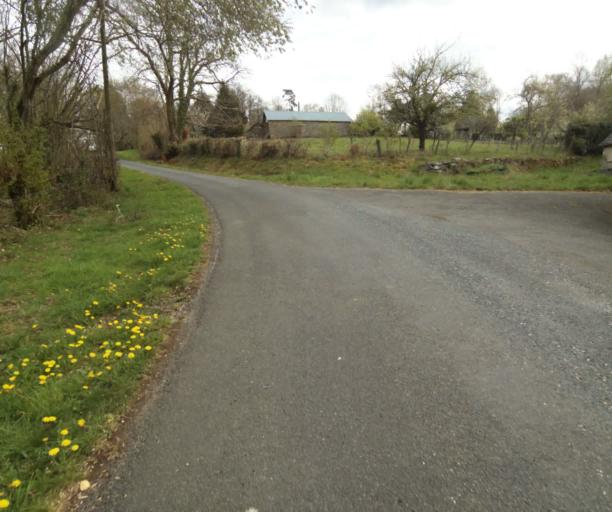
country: FR
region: Limousin
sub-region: Departement de la Correze
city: Laguenne
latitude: 45.2233
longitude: 1.8675
